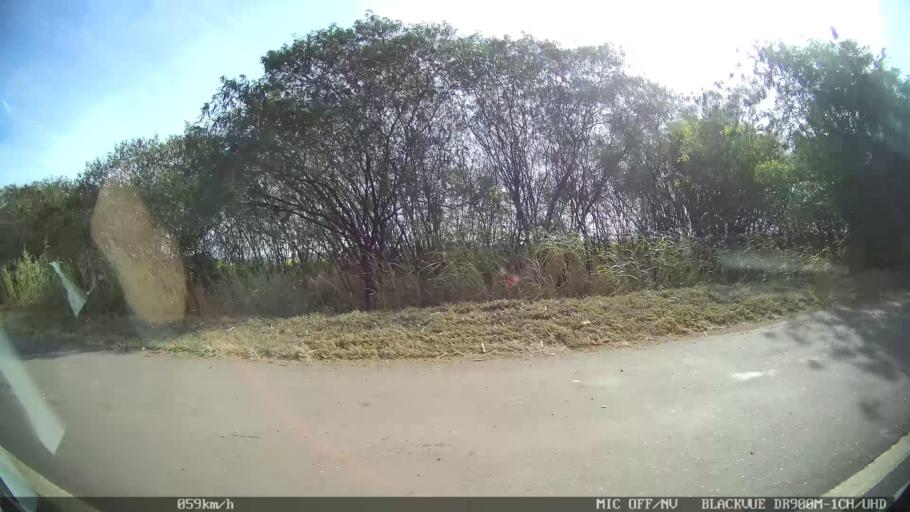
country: BR
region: Sao Paulo
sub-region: Rio Das Pedras
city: Rio das Pedras
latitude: -22.7948
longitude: -47.5880
